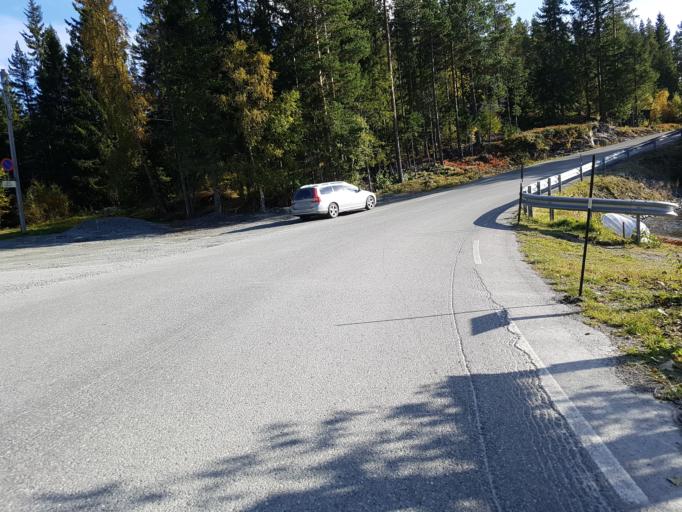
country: NO
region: Sor-Trondelag
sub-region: Malvik
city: Malvik
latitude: 63.3829
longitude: 10.5970
